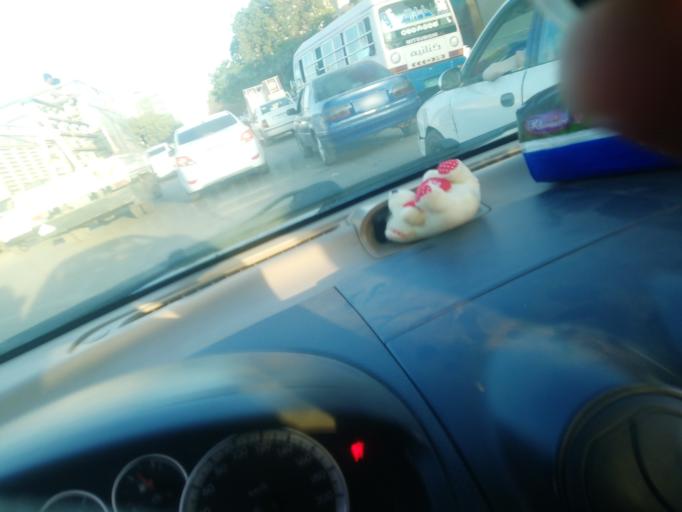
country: SD
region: Khartoum
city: Khartoum
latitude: 15.6060
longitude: 32.5320
